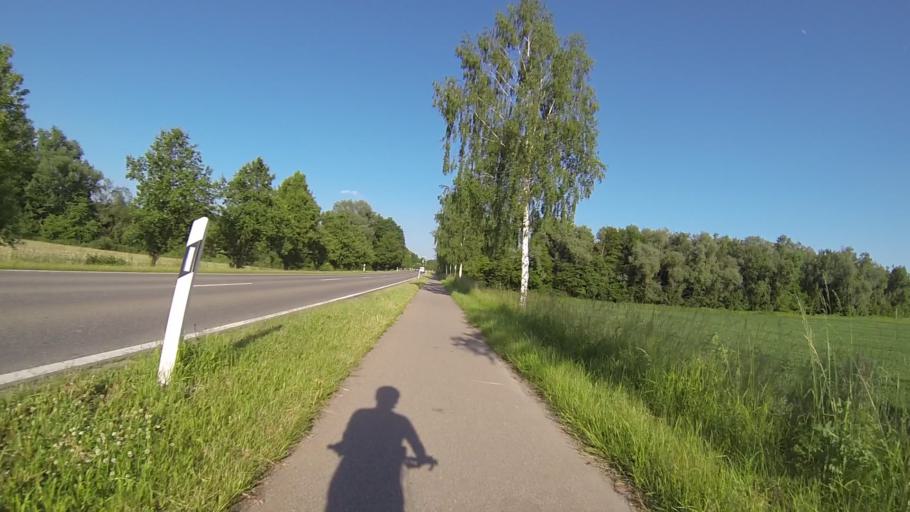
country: DE
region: Baden-Wuerttemberg
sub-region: Tuebingen Region
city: Laupheim
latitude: 48.2184
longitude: 9.8817
